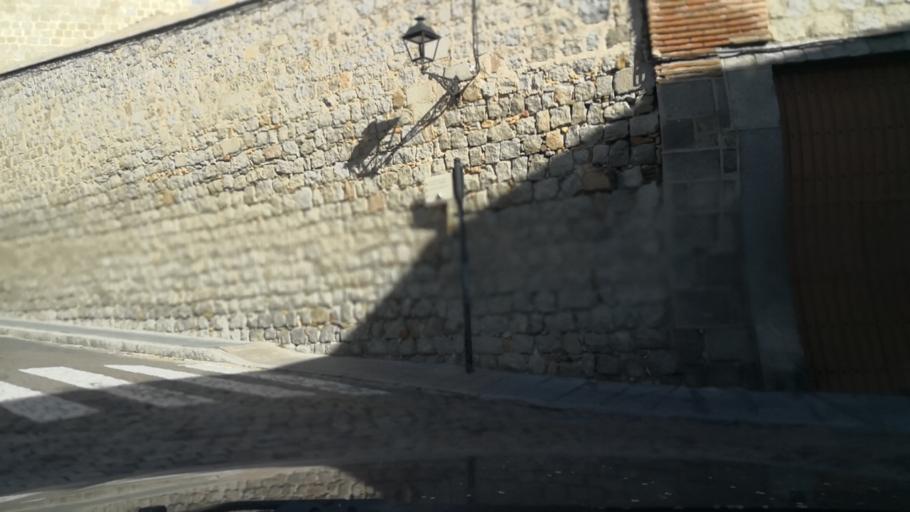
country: ES
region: Castille and Leon
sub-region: Provincia de Avila
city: Avila
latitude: 40.6528
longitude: -4.6977
